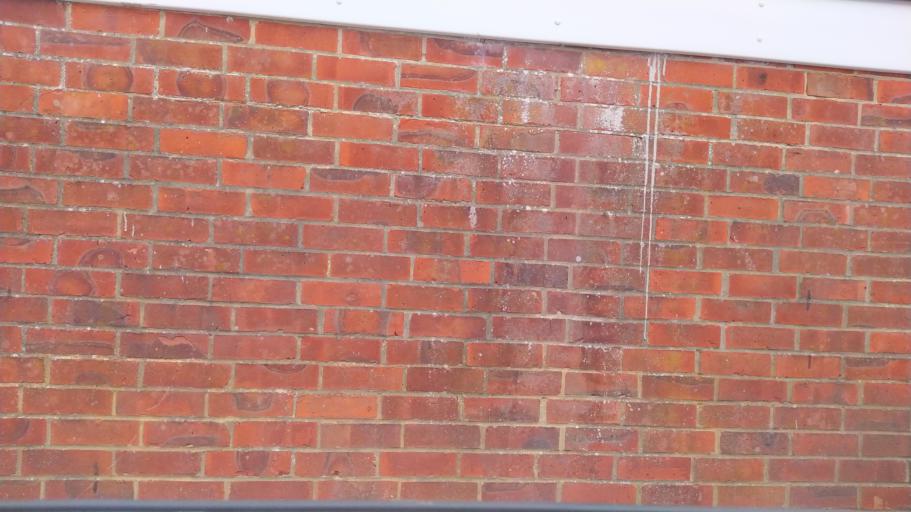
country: GB
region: England
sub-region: Hampshire
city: Ringwood
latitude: 50.8463
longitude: -1.7917
